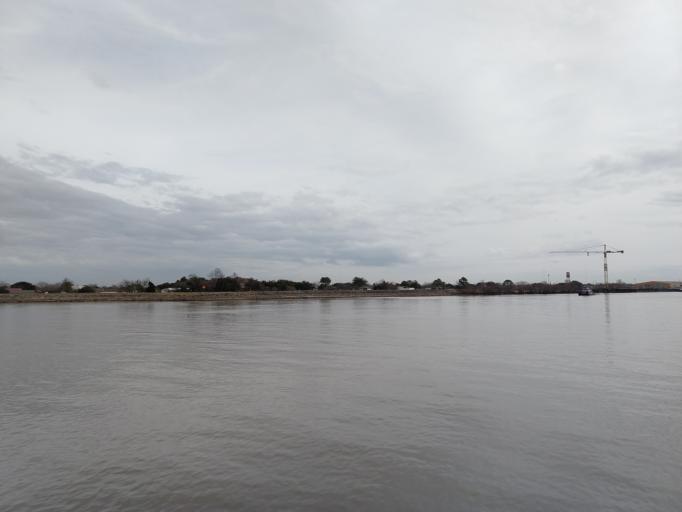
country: US
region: Louisiana
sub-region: Saint Bernard Parish
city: Arabi
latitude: 29.9553
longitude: -90.0295
